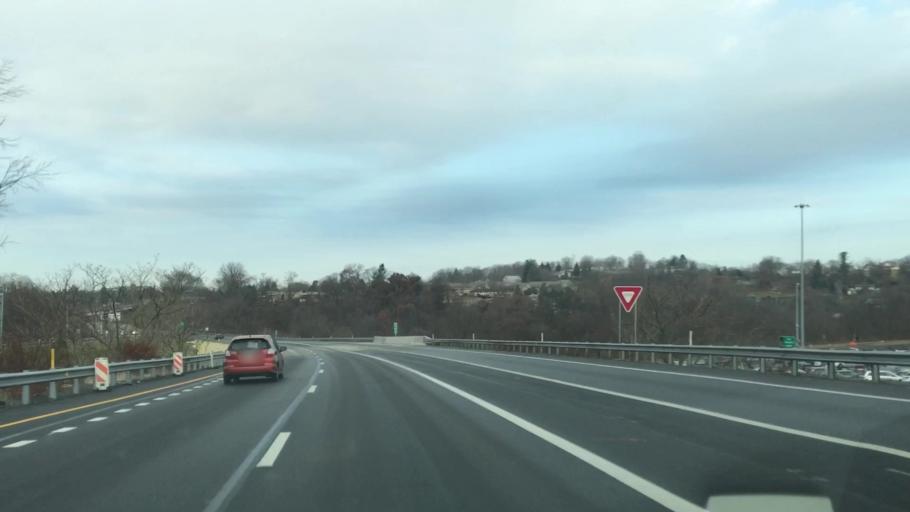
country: US
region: Pennsylvania
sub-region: Allegheny County
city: West View
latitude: 40.5054
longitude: -80.0302
